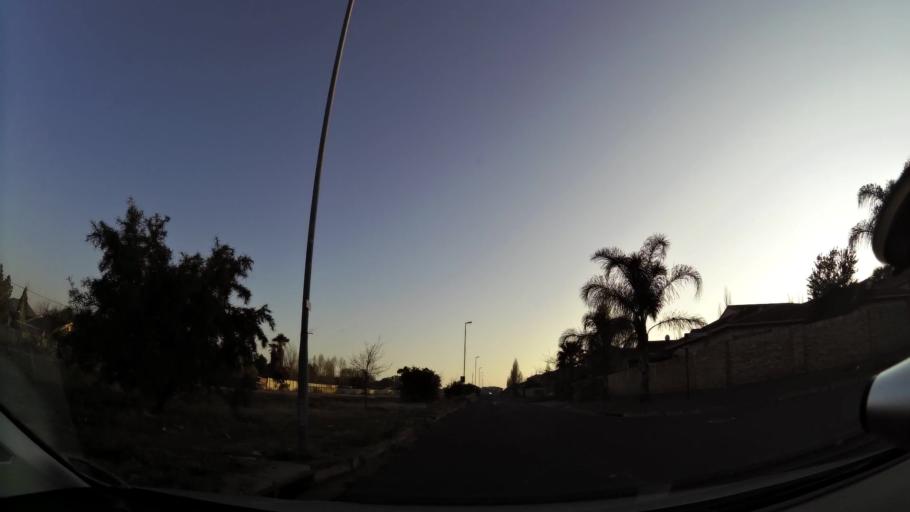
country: ZA
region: Orange Free State
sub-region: Mangaung Metropolitan Municipality
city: Bloemfontein
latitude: -29.0985
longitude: 26.1637
